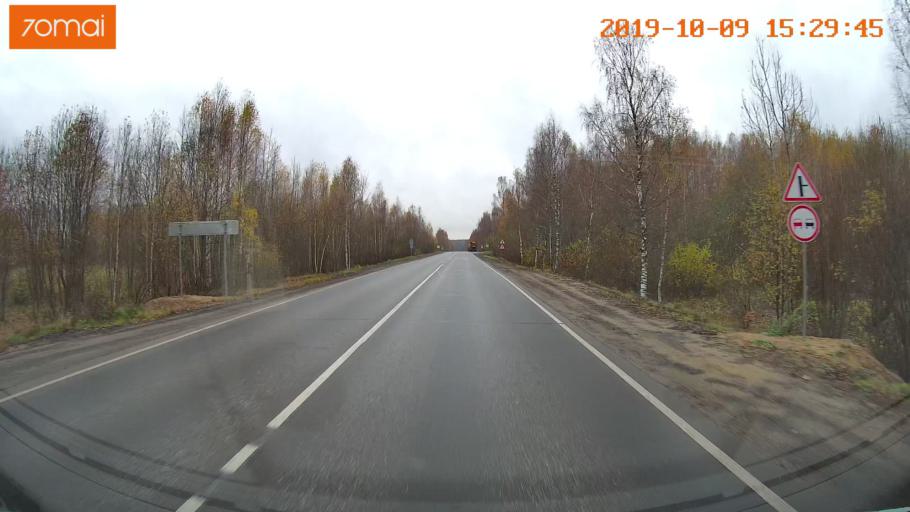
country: RU
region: Kostroma
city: Susanino
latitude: 57.9877
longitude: 41.3373
